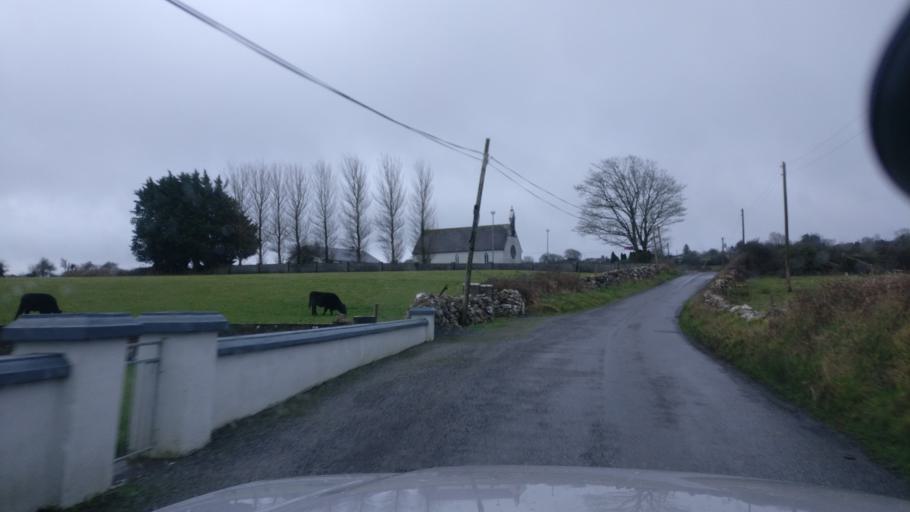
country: IE
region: Connaught
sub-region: County Galway
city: Loughrea
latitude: 53.1756
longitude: -8.6499
